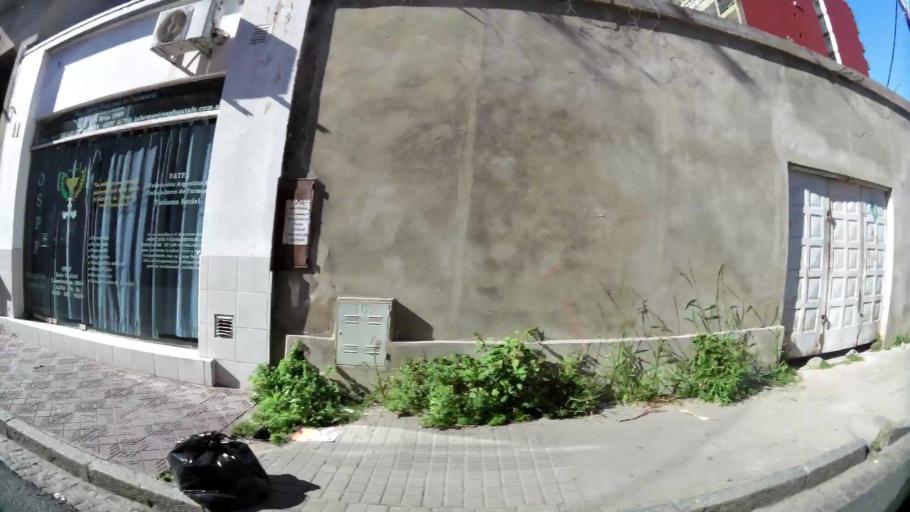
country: AR
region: Santa Fe
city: Santa Fe de la Vera Cruz
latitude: -31.6448
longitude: -60.7101
